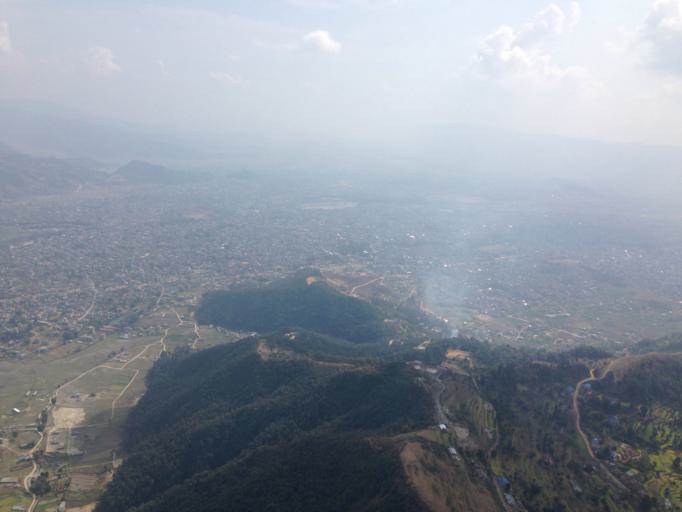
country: NP
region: Western Region
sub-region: Gandaki Zone
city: Pokhara
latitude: 28.2429
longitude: 83.9634
